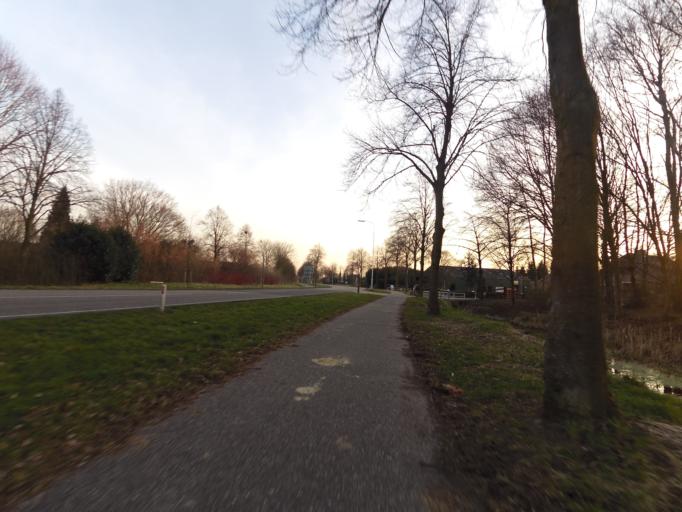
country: NL
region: Gelderland
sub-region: Gemeente Zevenaar
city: Zevenaar
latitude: 51.9373
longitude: 6.1209
